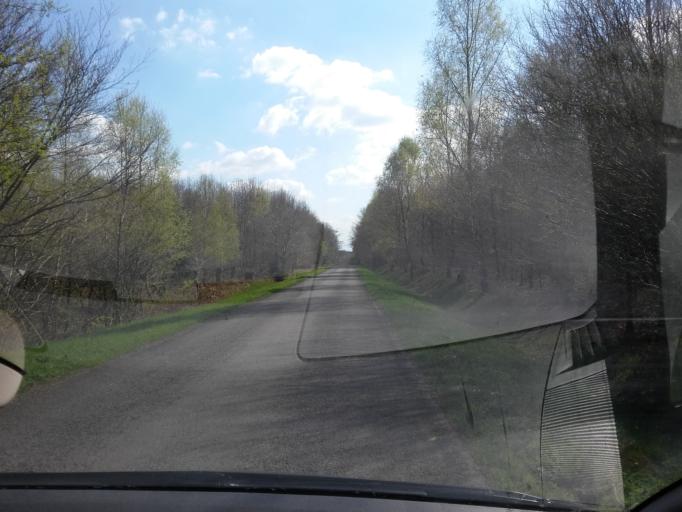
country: BE
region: Wallonia
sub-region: Province du Luxembourg
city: Habay-la-Vieille
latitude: 49.7370
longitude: 5.6590
